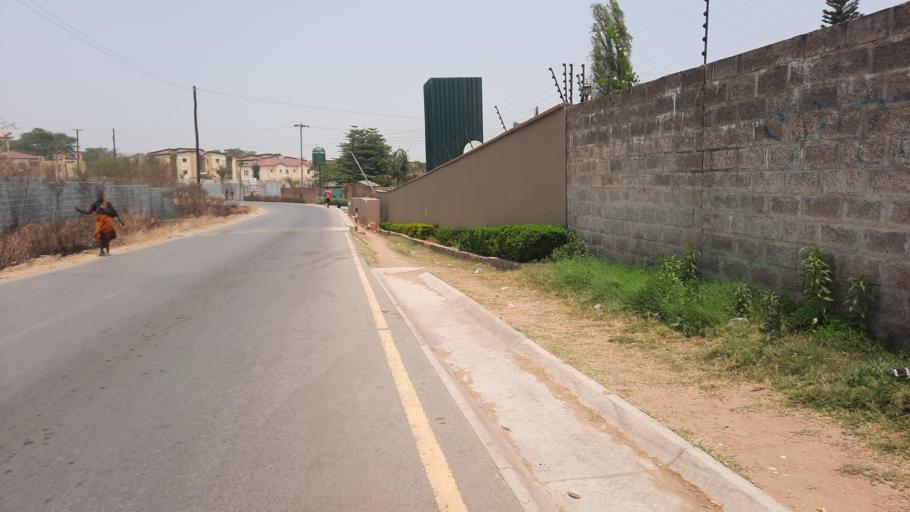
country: ZM
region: Lusaka
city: Lusaka
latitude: -15.4120
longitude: 28.3626
